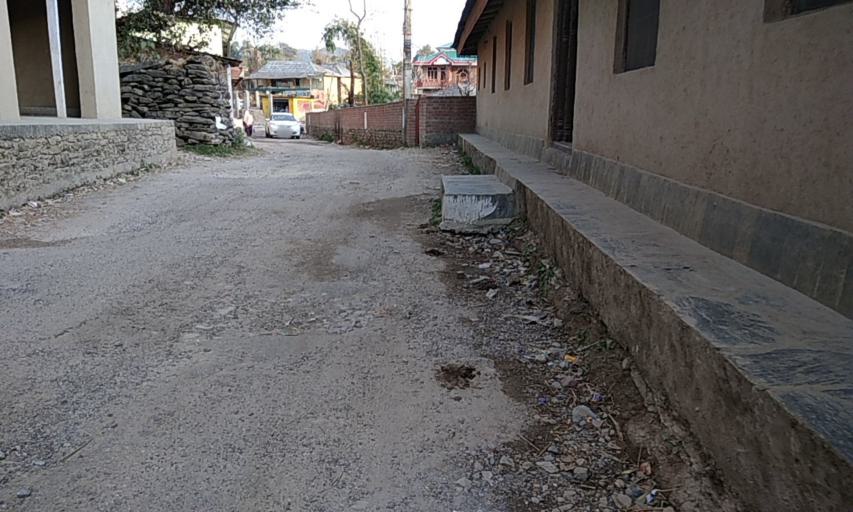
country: IN
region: Himachal Pradesh
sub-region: Kangra
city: Palampur
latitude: 32.1129
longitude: 76.5771
